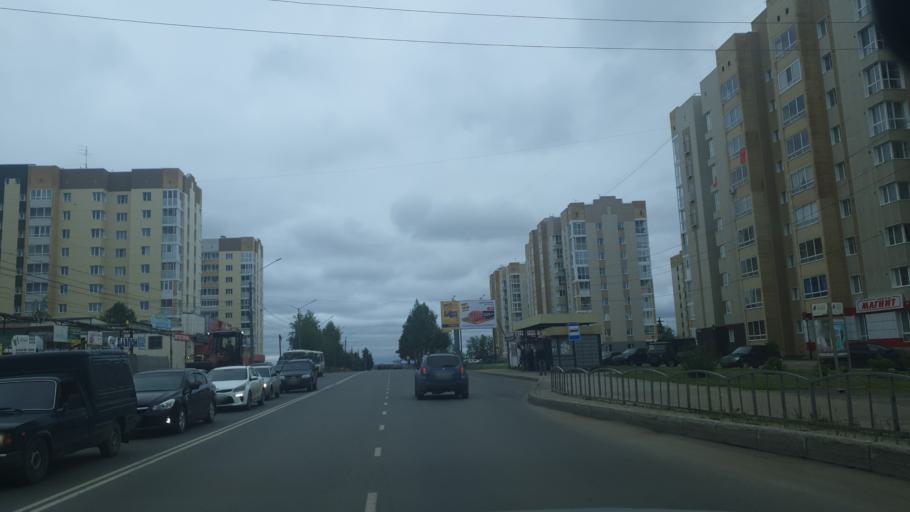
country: RU
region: Komi Republic
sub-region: Syktyvdinskiy Rayon
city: Syktyvkar
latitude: 61.6415
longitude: 50.8094
